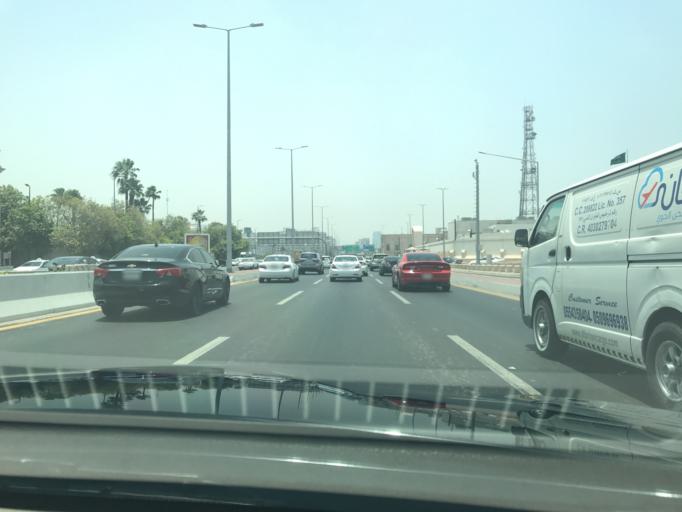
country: SA
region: Makkah
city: Jeddah
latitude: 21.5351
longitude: 39.1782
